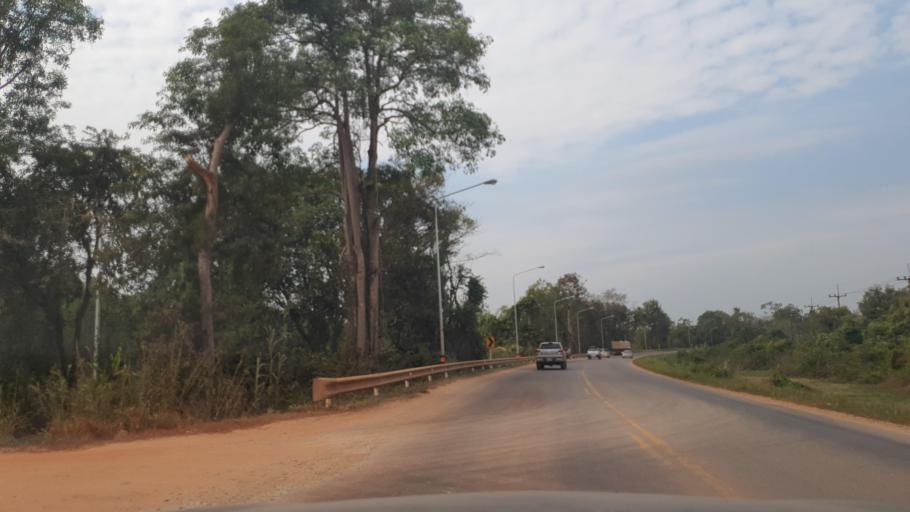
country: TH
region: Changwat Bueng Kan
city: Si Wilai
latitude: 18.2721
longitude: 103.8363
